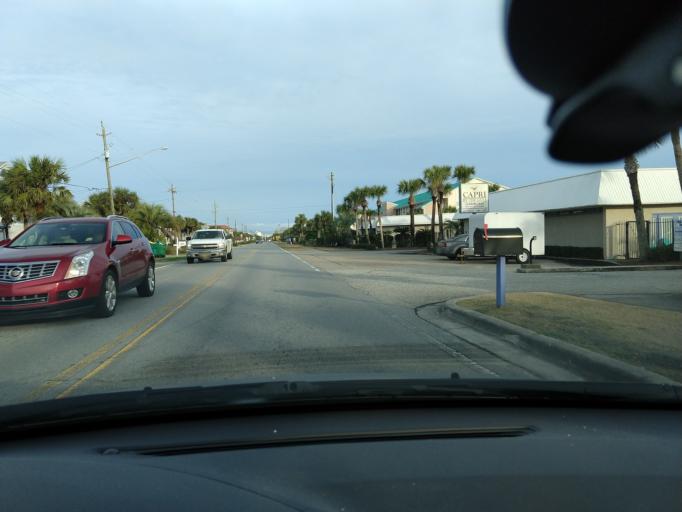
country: US
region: Florida
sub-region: Walton County
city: Miramar Beach
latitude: 30.3821
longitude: -86.4203
